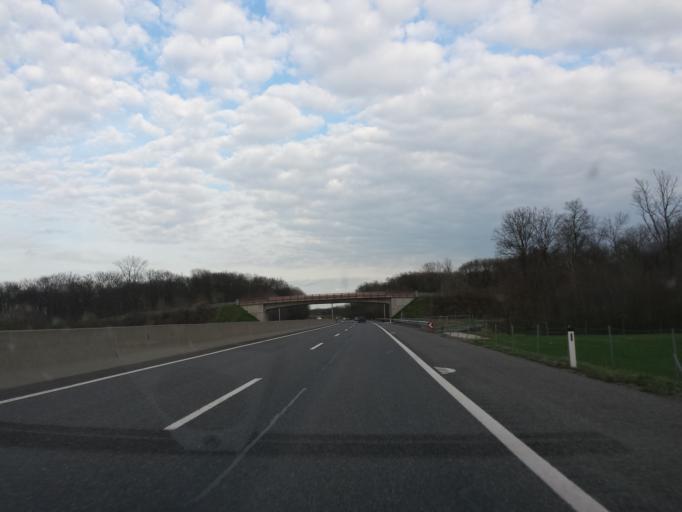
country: AT
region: Lower Austria
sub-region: Politischer Bezirk Korneuburg
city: Stetteldorf am Wagram
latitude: 48.3589
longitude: 15.9934
